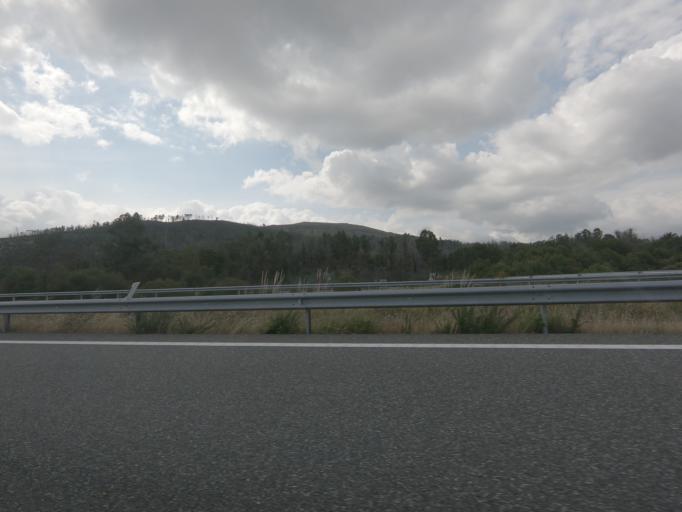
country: ES
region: Galicia
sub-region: Provincia de Ourense
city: Melon
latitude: 42.2694
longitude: -8.2072
